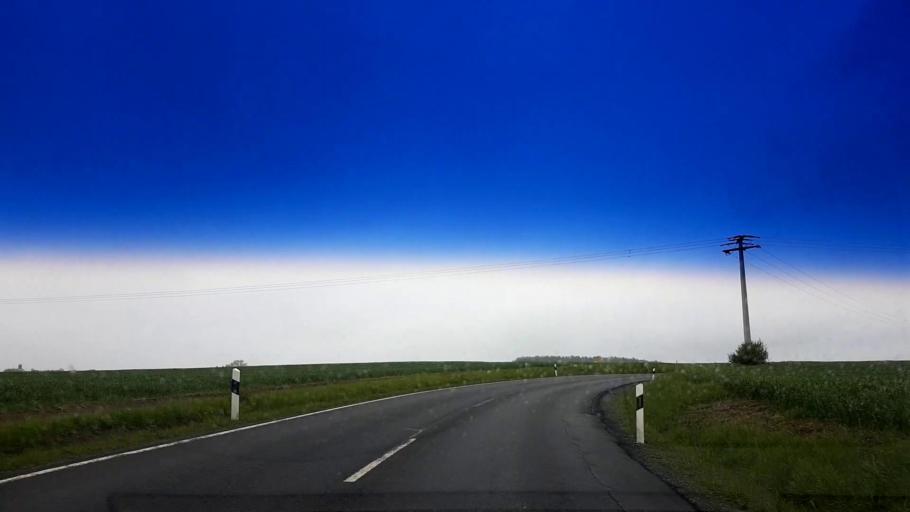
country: DE
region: Bavaria
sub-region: Upper Franconia
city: Bindlach
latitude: 50.0052
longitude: 11.6301
